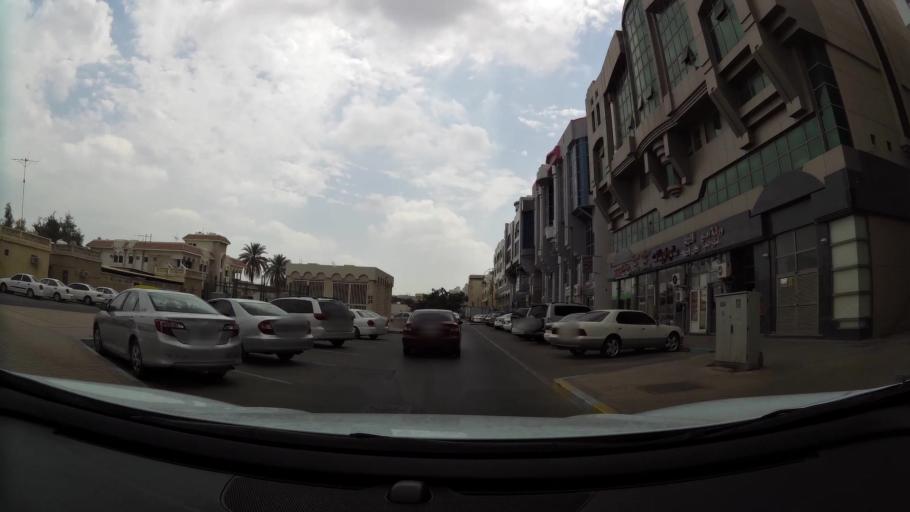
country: AE
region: Abu Dhabi
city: Al Ain
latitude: 24.2187
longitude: 55.7762
